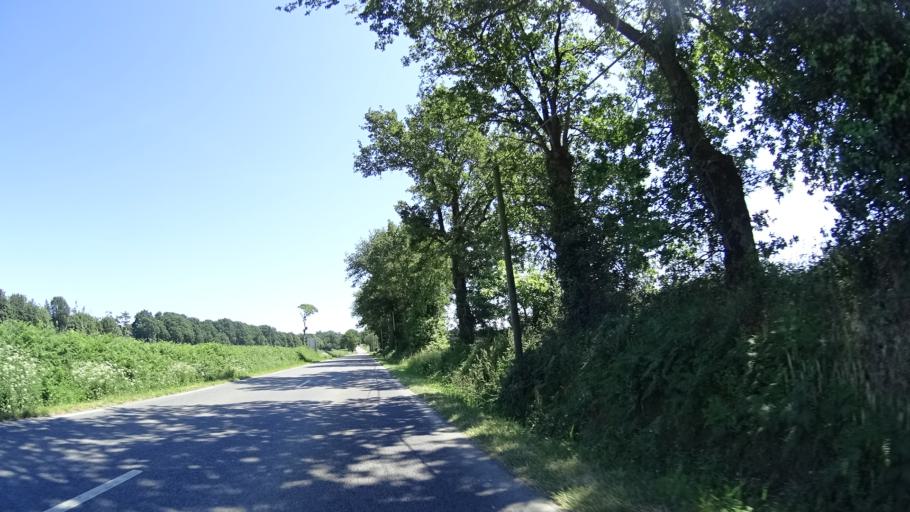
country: FR
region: Brittany
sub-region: Departement d'Ille-et-Vilaine
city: Bain-de-Bretagne
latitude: 47.8416
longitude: -1.7171
